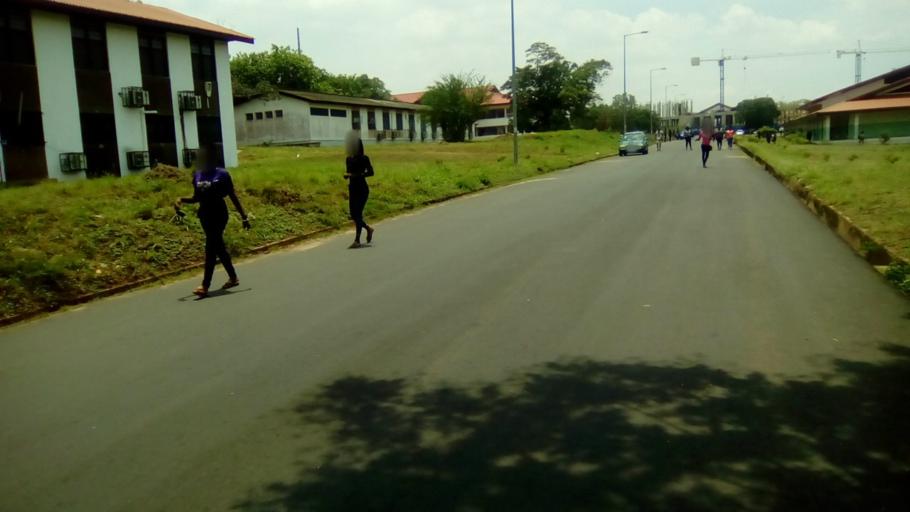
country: GH
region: Greater Accra
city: Medina Estates
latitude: 5.6557
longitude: -0.1866
